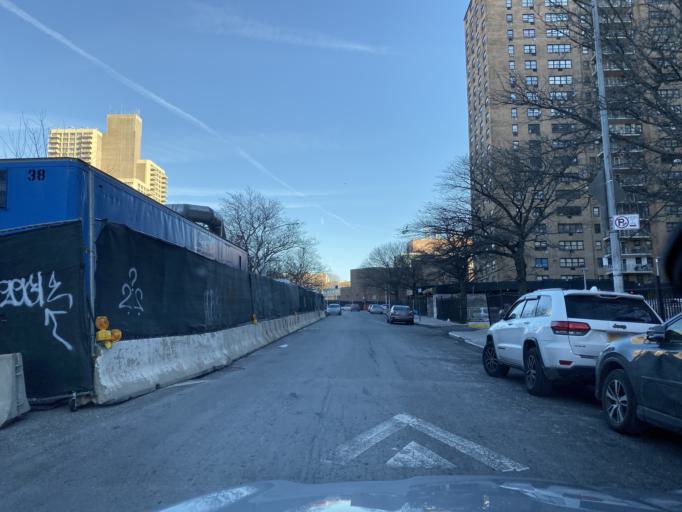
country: US
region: New York
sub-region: Kings County
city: Brooklyn
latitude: 40.6652
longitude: -73.9589
